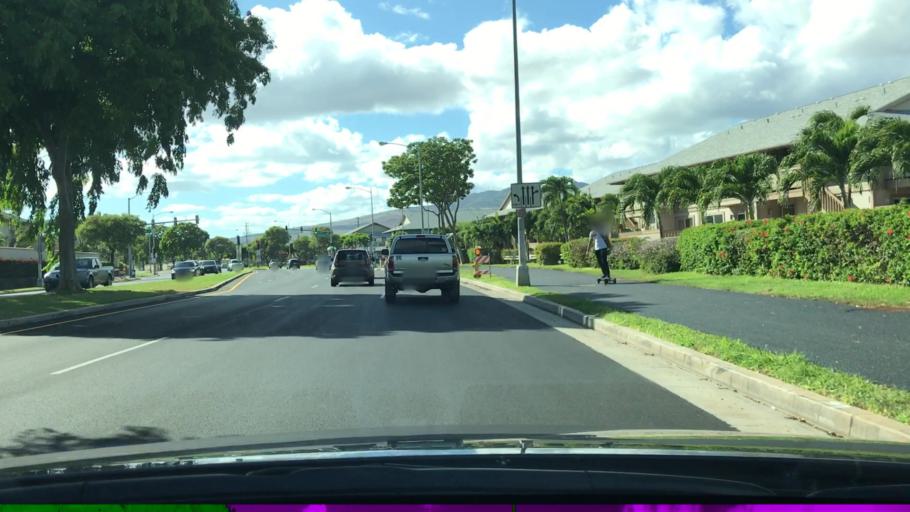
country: US
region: Hawaii
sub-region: Honolulu County
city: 'Ewa Gentry
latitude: 21.3370
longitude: -158.0311
